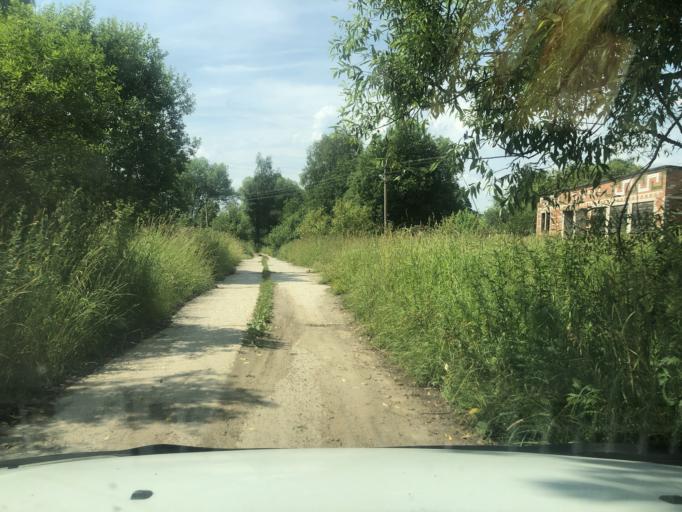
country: RU
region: Jaroslavl
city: Pereslavl'-Zalesskiy
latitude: 57.0457
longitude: 38.8687
